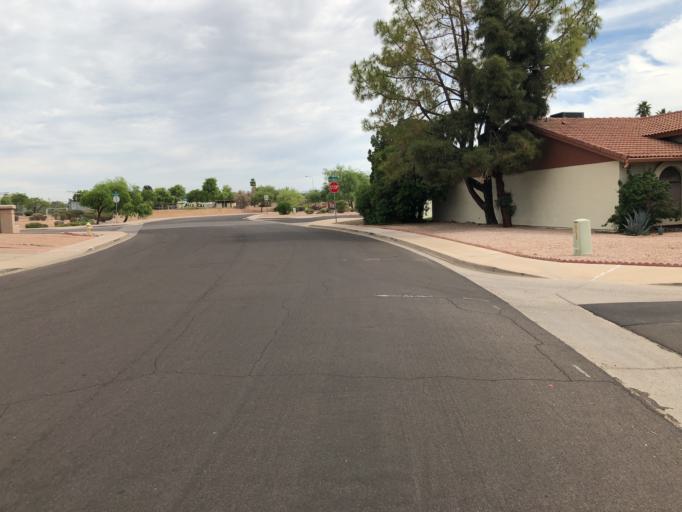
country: US
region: Arizona
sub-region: Maricopa County
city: Tempe
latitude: 33.4581
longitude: -111.8969
